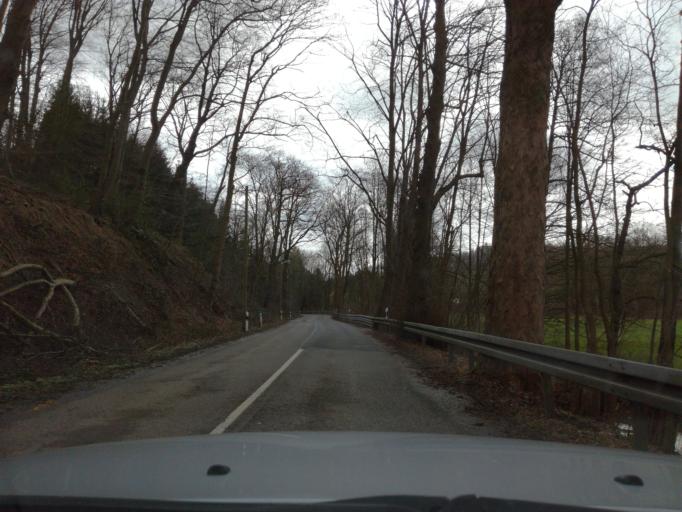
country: DE
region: North Rhine-Westphalia
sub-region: Regierungsbezirk Dusseldorf
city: Velbert
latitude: 51.3717
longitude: 7.0392
